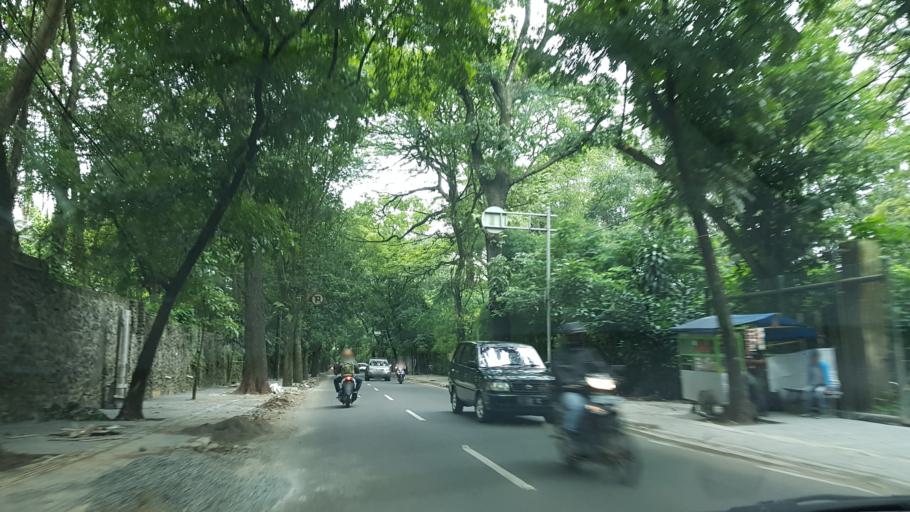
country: ID
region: West Java
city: Bandung
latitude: -6.8897
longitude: 107.6081
